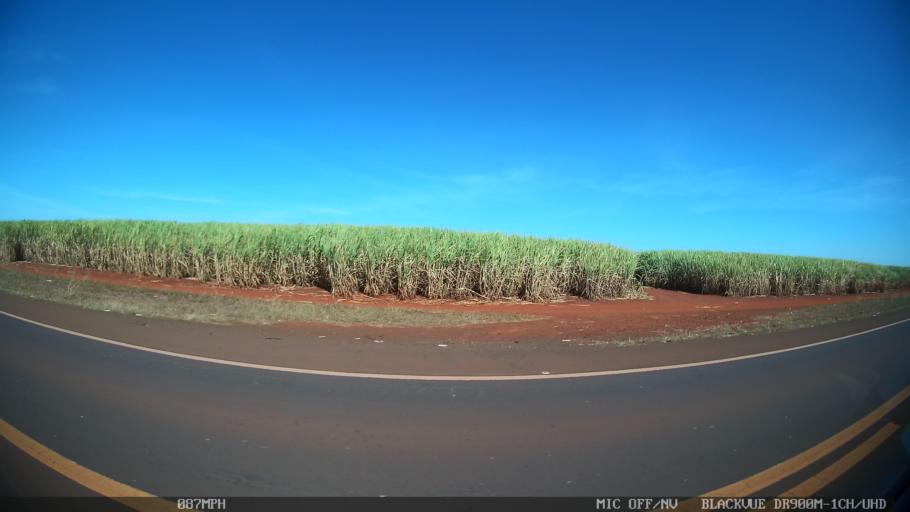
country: BR
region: Sao Paulo
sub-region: Guaira
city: Guaira
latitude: -20.4447
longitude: -48.2595
